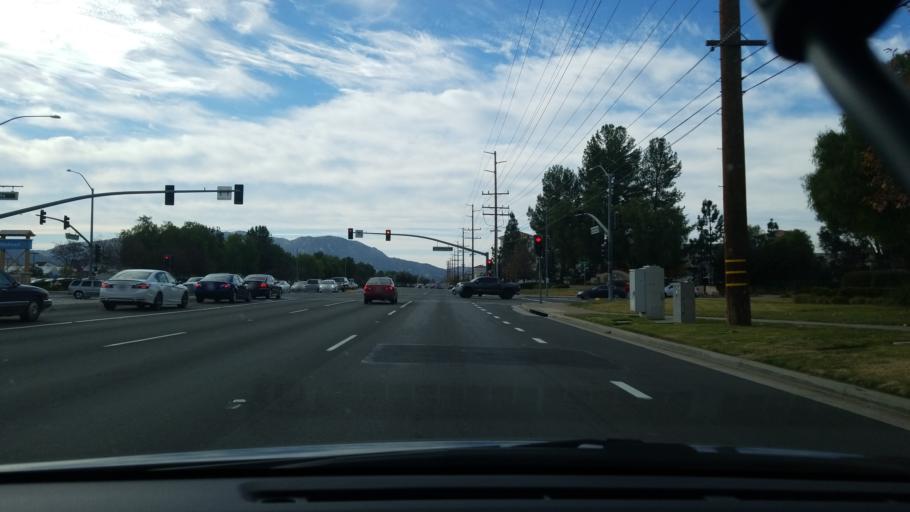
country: US
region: California
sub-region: Riverside County
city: Temecula
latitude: 33.4826
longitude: -117.0931
